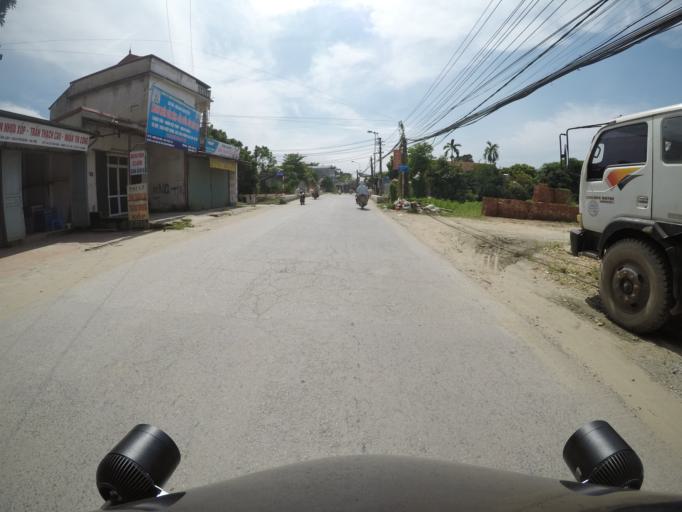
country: VN
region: Ha Noi
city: Troi
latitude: 21.0782
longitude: 105.7100
